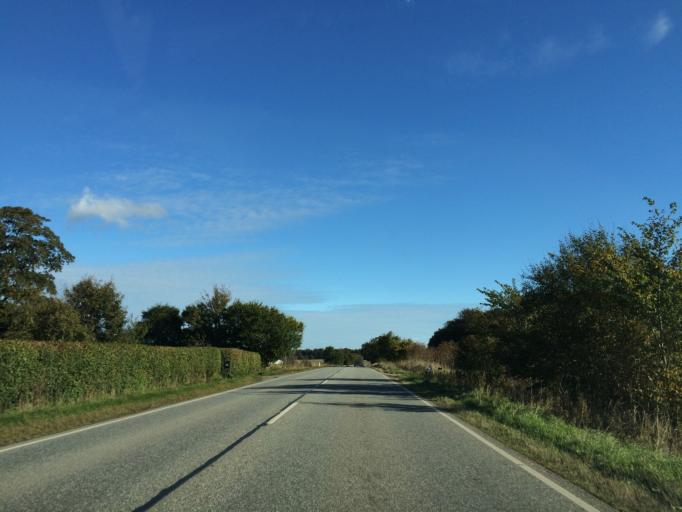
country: DK
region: Central Jutland
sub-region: Randers Kommune
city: Langa
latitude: 56.3908
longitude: 9.9696
